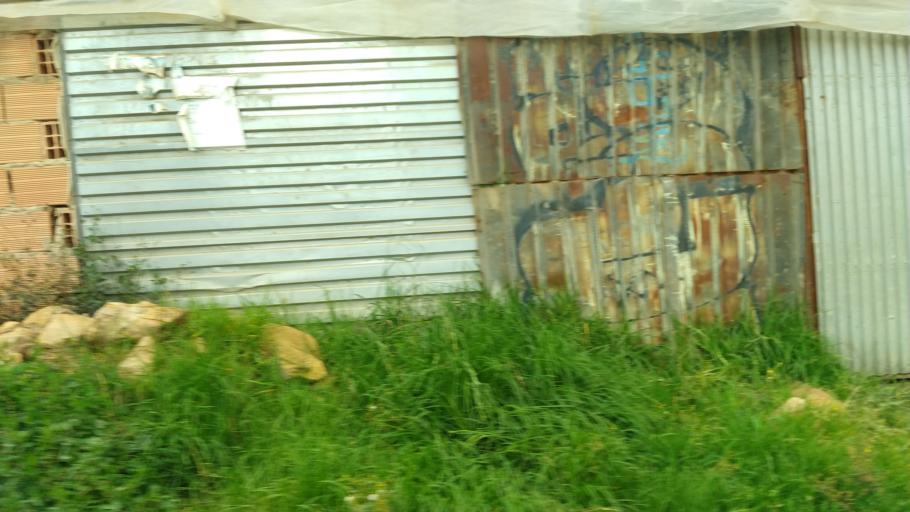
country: CO
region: Cundinamarca
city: Soacha
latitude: 4.5582
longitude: -74.2127
